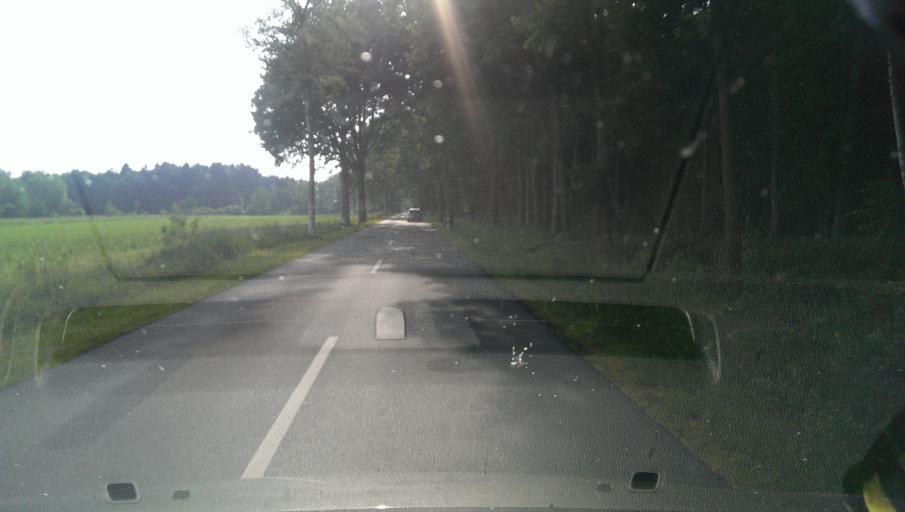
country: DE
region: Lower Saxony
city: Wietzendorf
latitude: 52.9146
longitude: 10.0424
